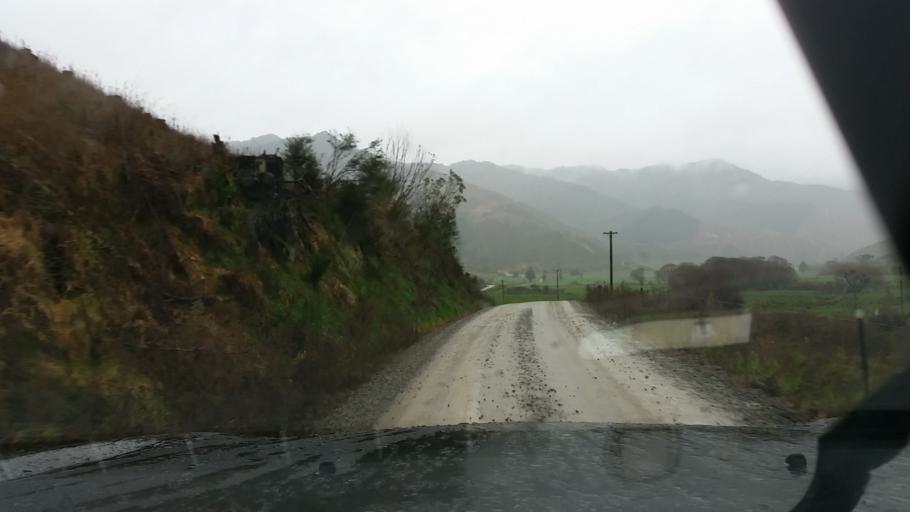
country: NZ
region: Marlborough
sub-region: Marlborough District
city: Picton
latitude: -41.3498
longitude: 173.9298
